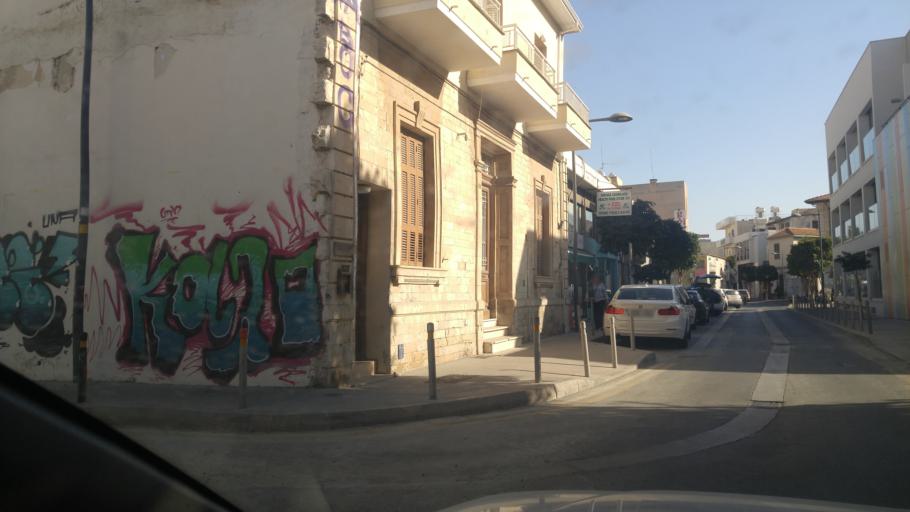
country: CY
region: Limassol
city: Limassol
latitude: 34.6751
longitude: 33.0421
